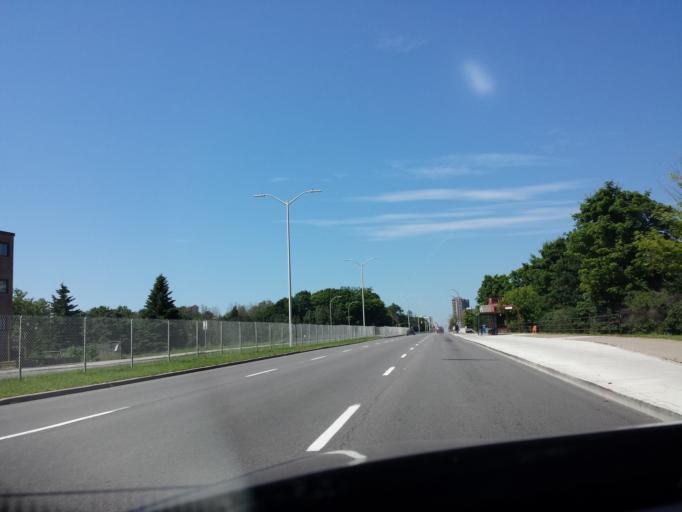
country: CA
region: Ontario
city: Bells Corners
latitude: 45.3656
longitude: -75.7814
